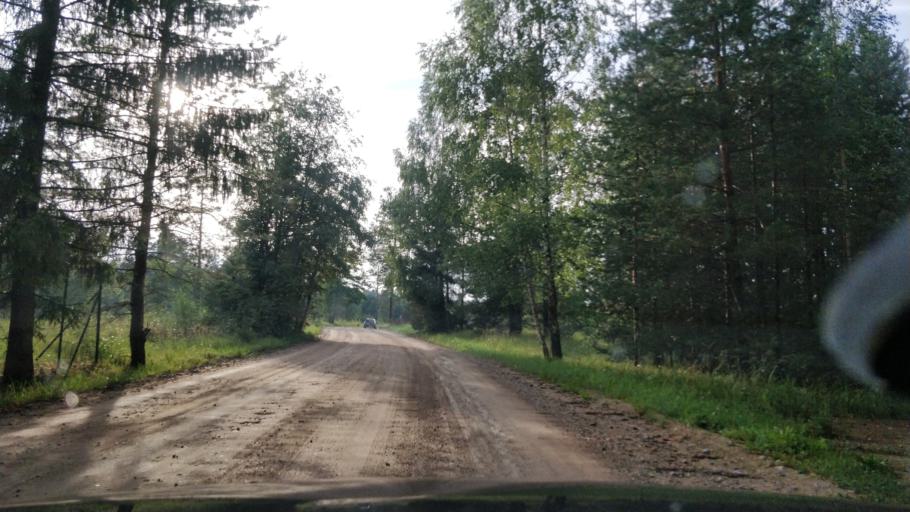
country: LV
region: Incukalns
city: Incukalns
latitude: 57.0938
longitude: 24.7631
